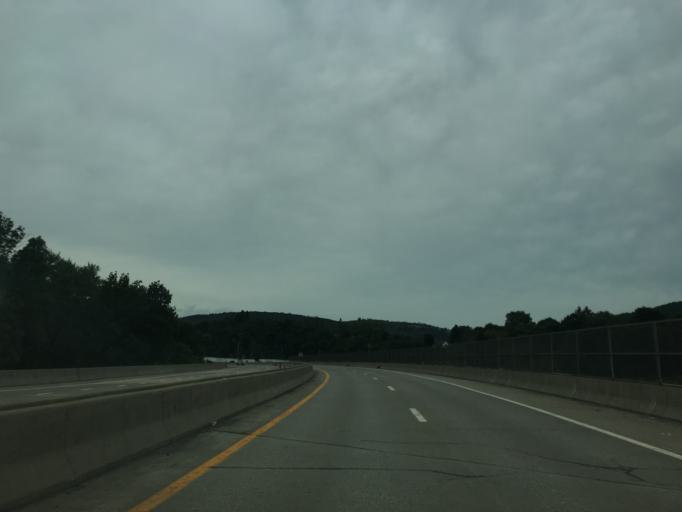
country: US
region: New York
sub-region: Broome County
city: Port Dickinson
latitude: 42.1430
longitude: -75.8953
